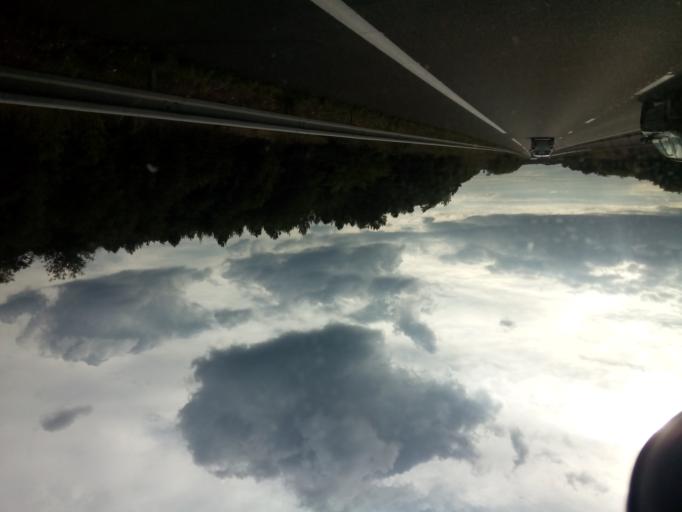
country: FR
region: Centre
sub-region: Departement du Loir-et-Cher
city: Faverolles-sur-Cher
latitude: 47.2937
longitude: 1.1718
